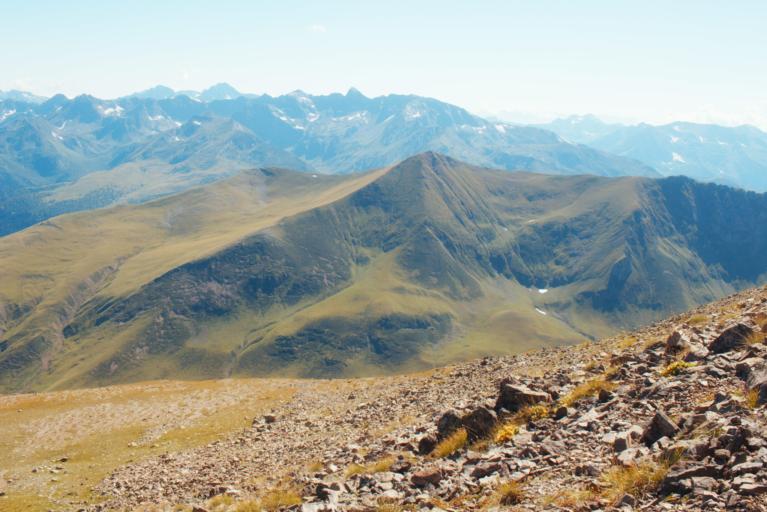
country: RU
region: Karachayevo-Cherkesiya
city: Mednogorskiy
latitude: 43.6190
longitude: 41.0950
